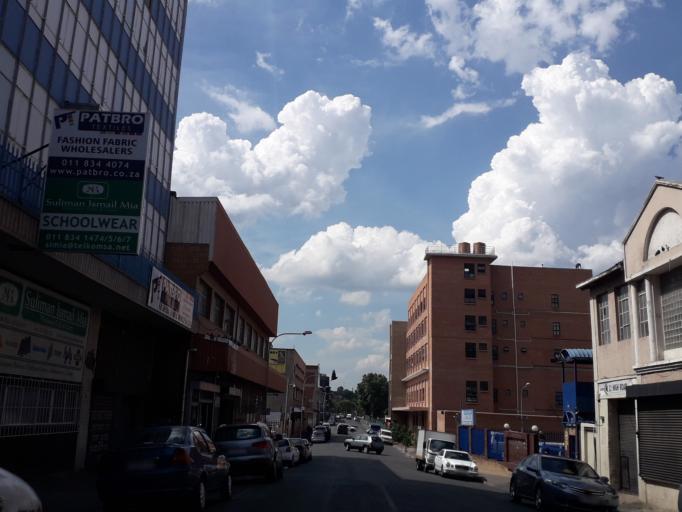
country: ZA
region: Gauteng
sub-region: City of Johannesburg Metropolitan Municipality
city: Johannesburg
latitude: -26.2072
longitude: 28.0233
